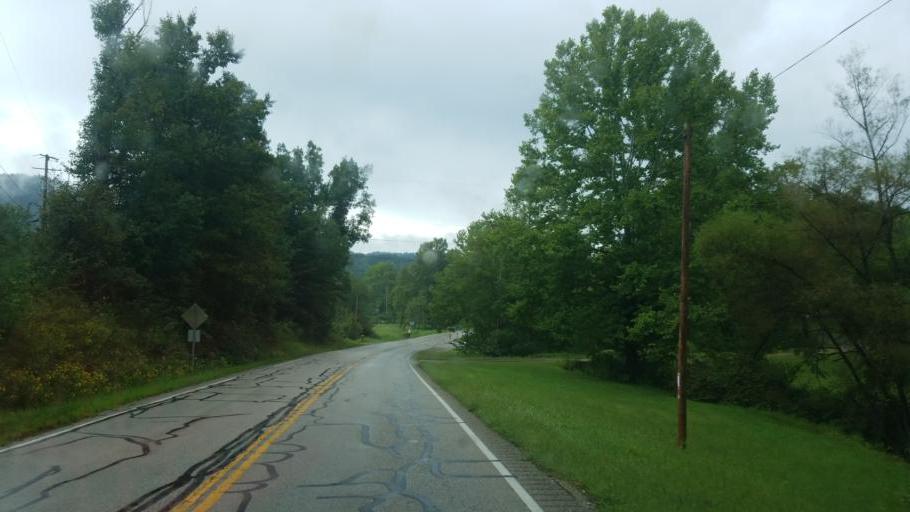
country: US
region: Kentucky
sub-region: Rowan County
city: Morehead
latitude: 38.1546
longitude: -83.4714
